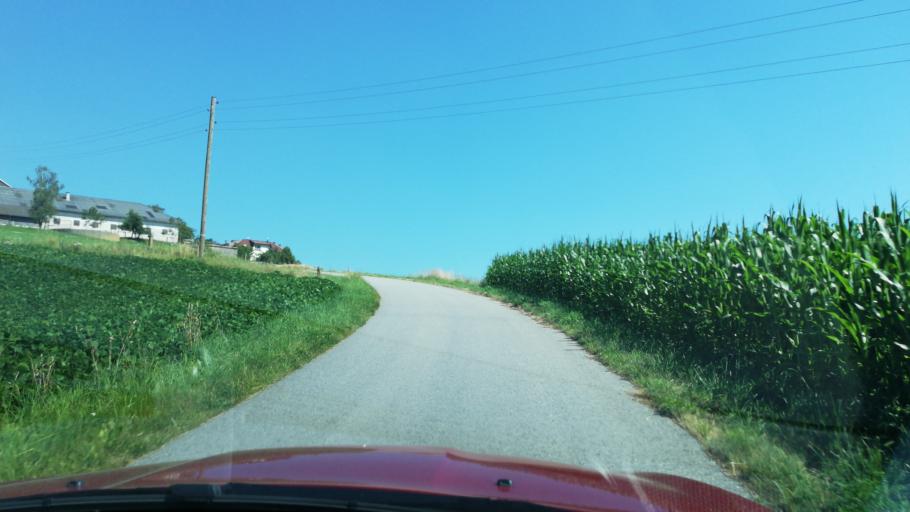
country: AT
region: Upper Austria
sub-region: Politischer Bezirk Rohrbach
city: Kleinzell im Muehlkreis
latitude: 48.4808
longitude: 14.0506
